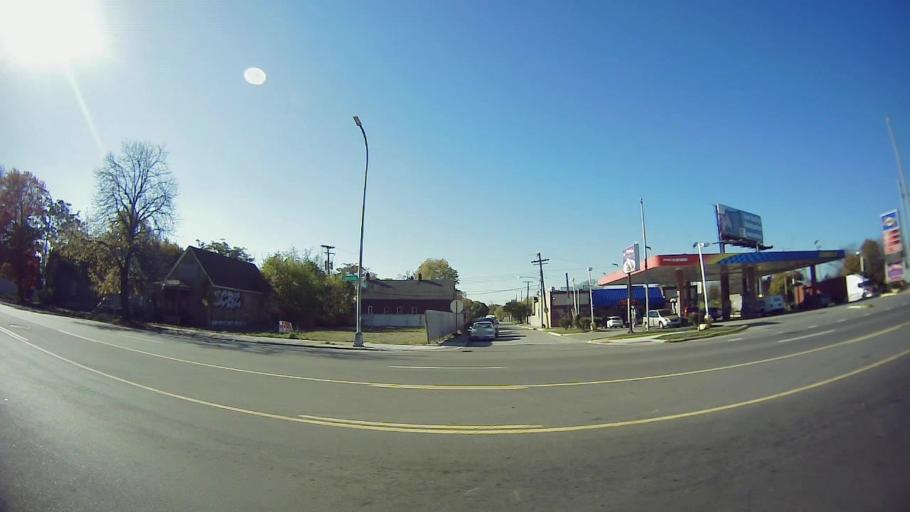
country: US
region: Michigan
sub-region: Wayne County
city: Dearborn
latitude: 42.3367
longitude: -83.1242
